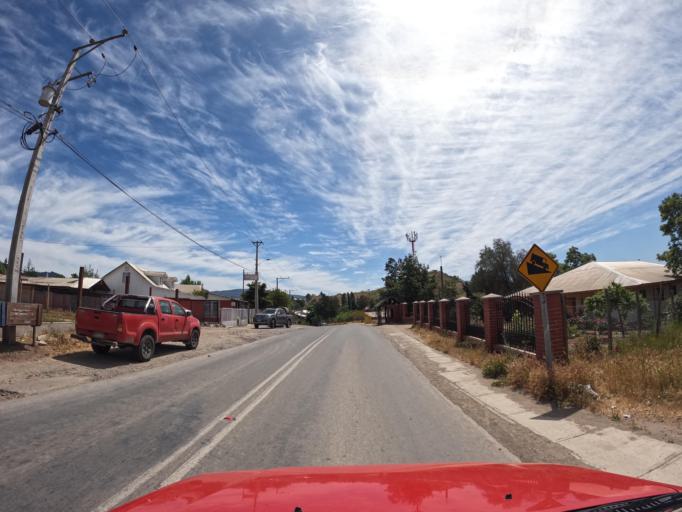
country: CL
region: Maule
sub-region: Provincia de Talca
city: Talca
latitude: -35.1202
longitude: -71.6801
